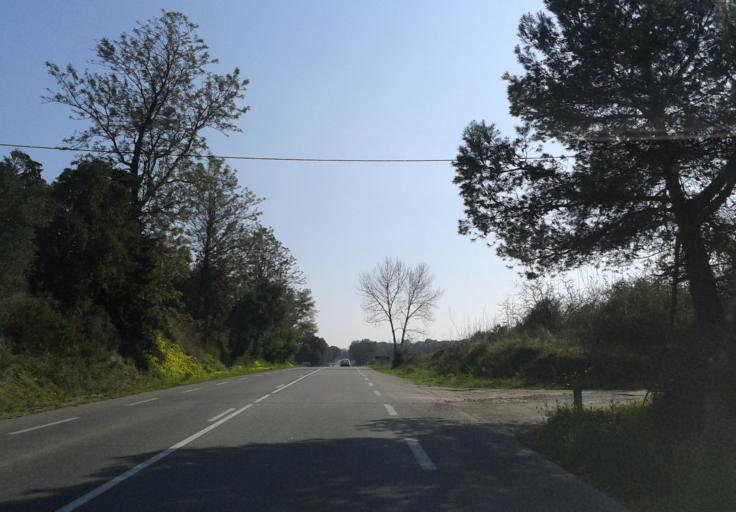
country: FR
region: Corsica
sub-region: Departement de la Haute-Corse
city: Linguizzetta
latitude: 42.2424
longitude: 9.5456
